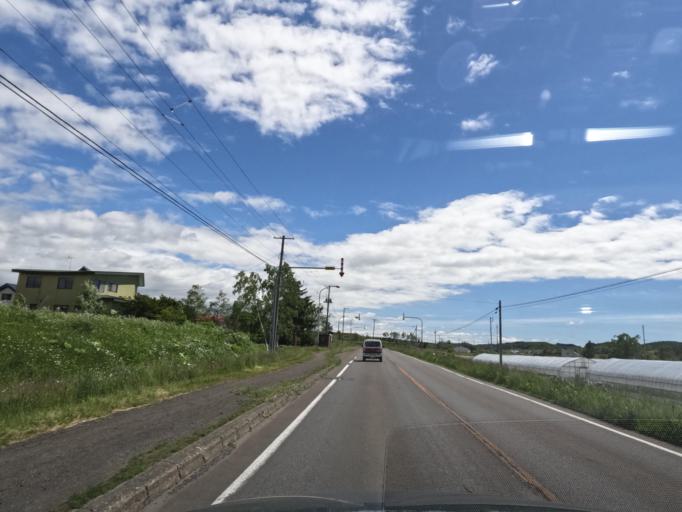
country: JP
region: Hokkaido
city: Iwamizawa
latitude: 43.1372
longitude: 141.8059
